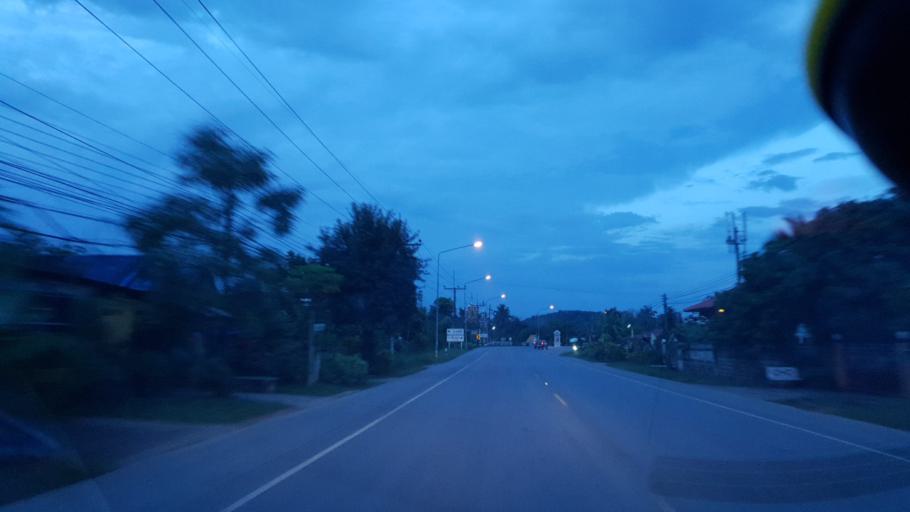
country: TH
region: Chiang Rai
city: Wiang Chiang Rung
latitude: 19.9854
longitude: 100.0263
